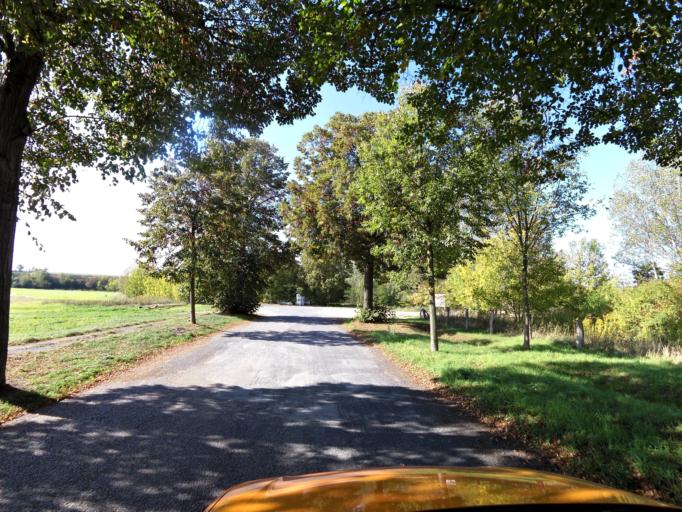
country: DE
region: Brandenburg
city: Grossbeeren
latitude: 52.3520
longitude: 13.2926
